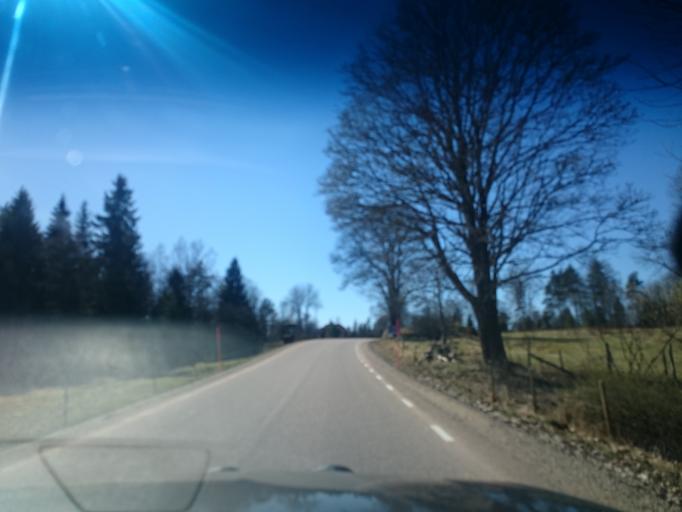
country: SE
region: Kronoberg
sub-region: Vaxjo Kommun
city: Braas
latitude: 57.2346
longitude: 15.0287
